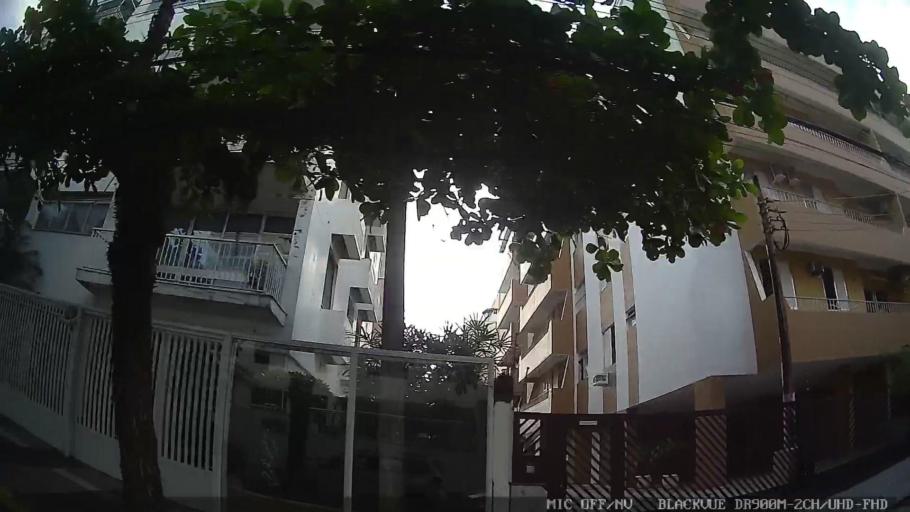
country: BR
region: Sao Paulo
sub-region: Guaruja
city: Guaruja
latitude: -23.9844
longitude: -46.2351
